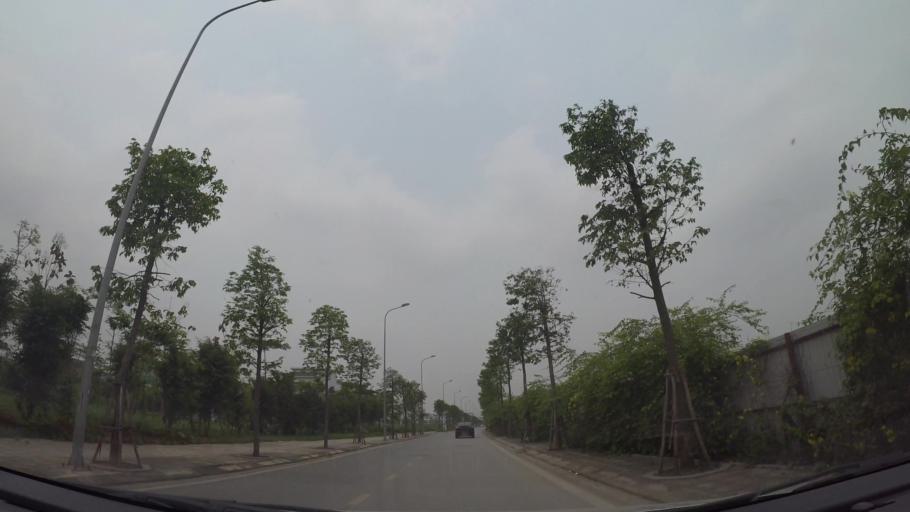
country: VN
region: Ha Noi
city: Cau Dien
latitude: 21.0254
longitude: 105.7463
